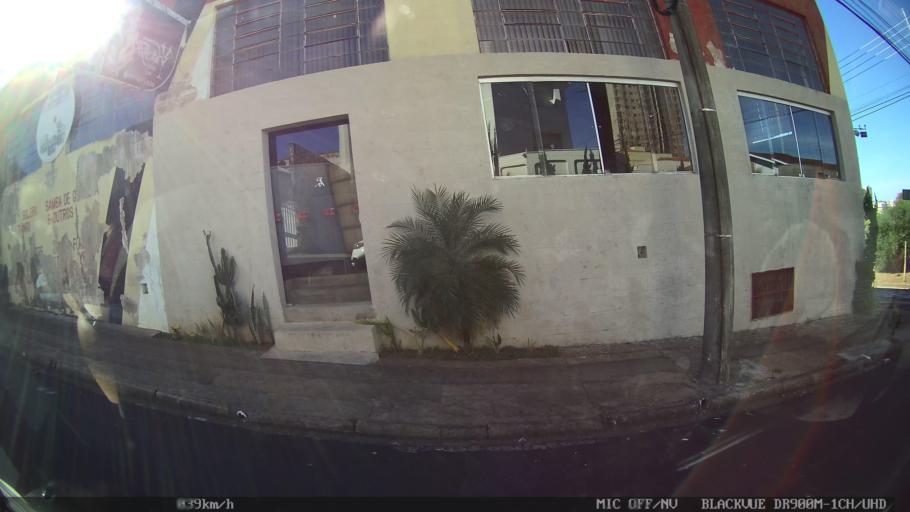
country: BR
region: Sao Paulo
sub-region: Franca
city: Franca
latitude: -20.5366
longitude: -47.4090
